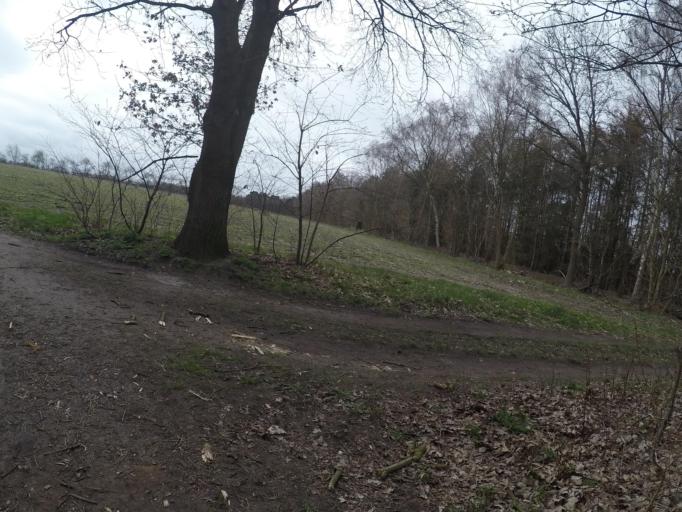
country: DE
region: Lower Saxony
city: Nordholz
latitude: 53.8037
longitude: 8.6163
